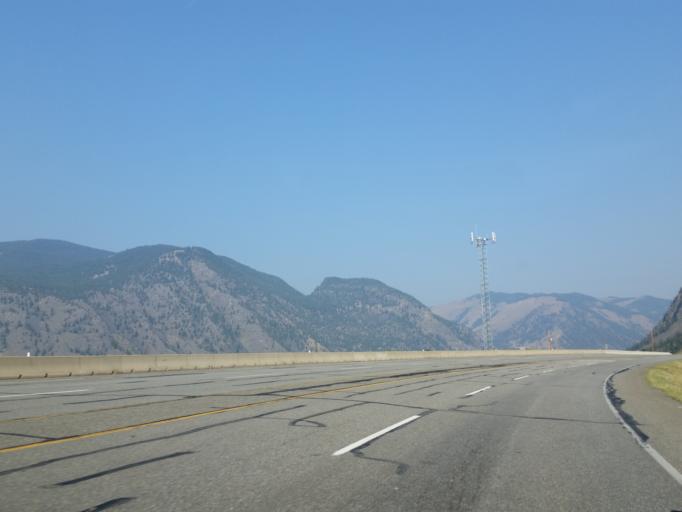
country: CA
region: British Columbia
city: Oliver
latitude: 49.2212
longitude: -119.9556
